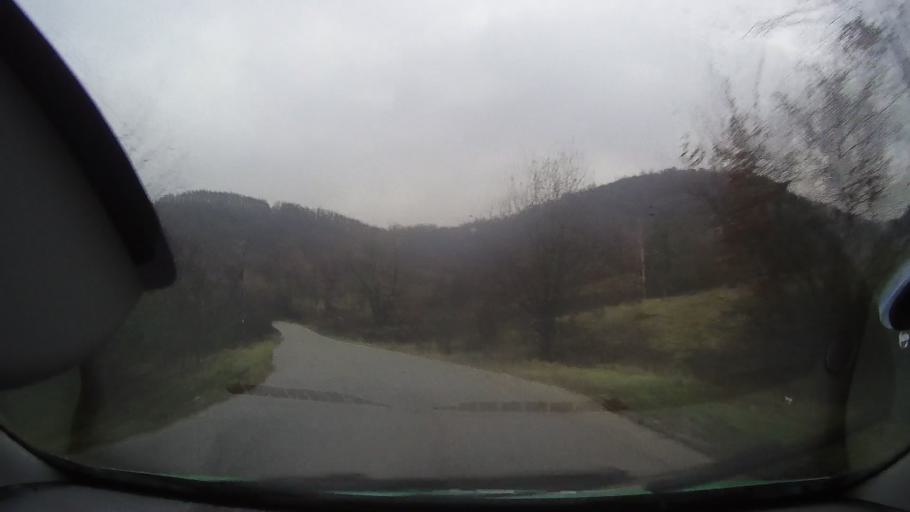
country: RO
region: Hunedoara
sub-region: Comuna Ribita
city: Ribita
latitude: 46.2330
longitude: 22.7465
